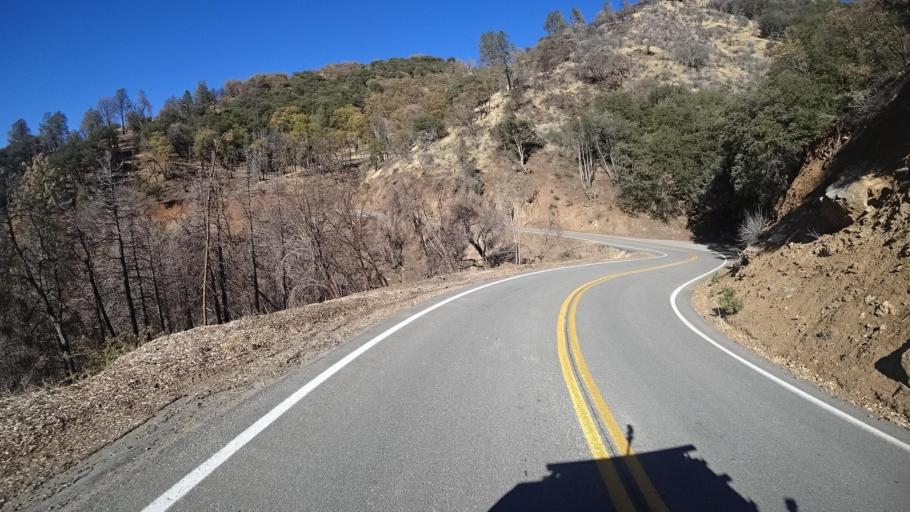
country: US
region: California
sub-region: Kern County
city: Alta Sierra
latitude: 35.7438
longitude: -118.5707
